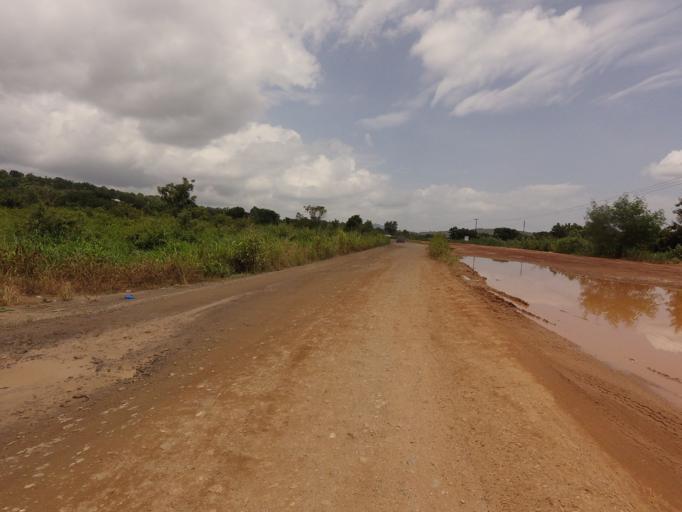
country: GH
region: Volta
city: Ho
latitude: 6.6781
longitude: 0.3160
